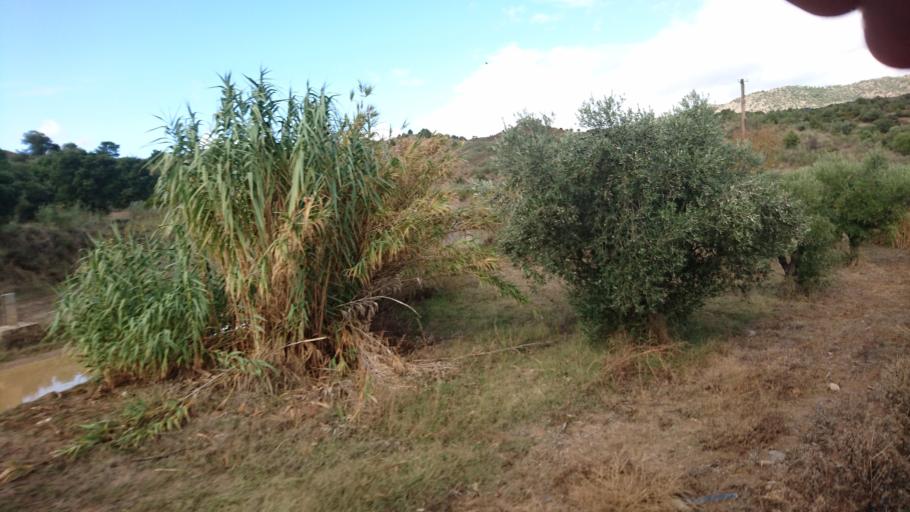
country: PT
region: Guarda
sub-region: Vila Nova de Foz Coa
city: Vila Nova de Foz Coa
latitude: 41.1293
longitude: -7.1373
